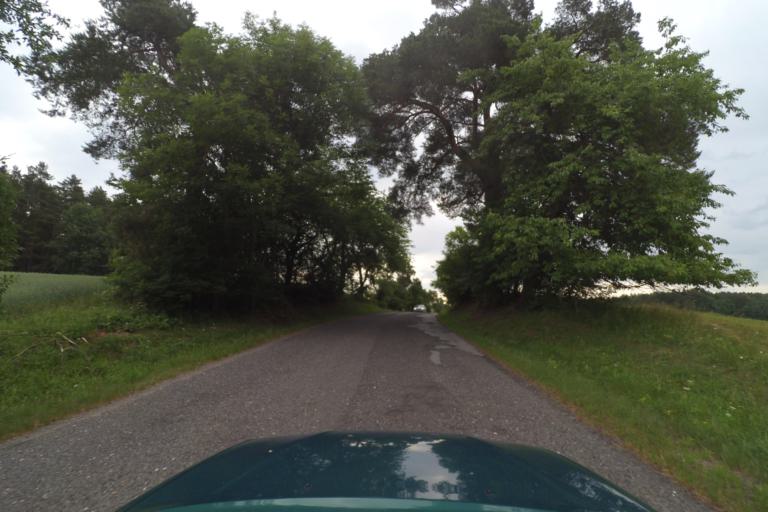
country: CZ
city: Cesky Dub
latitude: 50.6727
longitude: 15.0394
